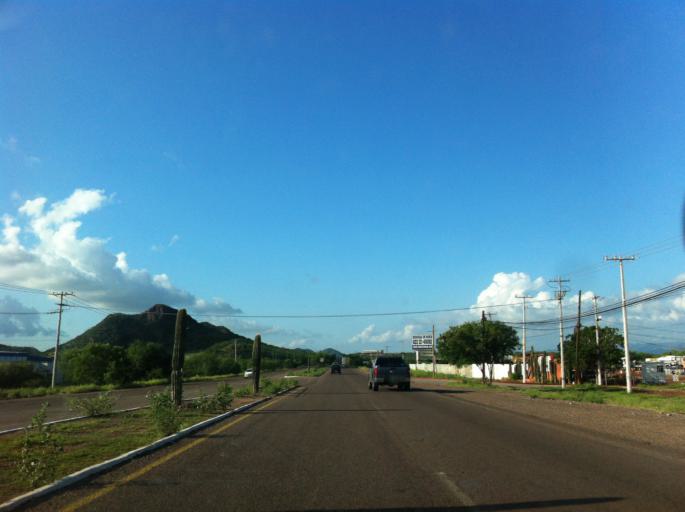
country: MX
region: Sonora
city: Heroica Guaymas
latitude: 27.9617
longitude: -110.9357
